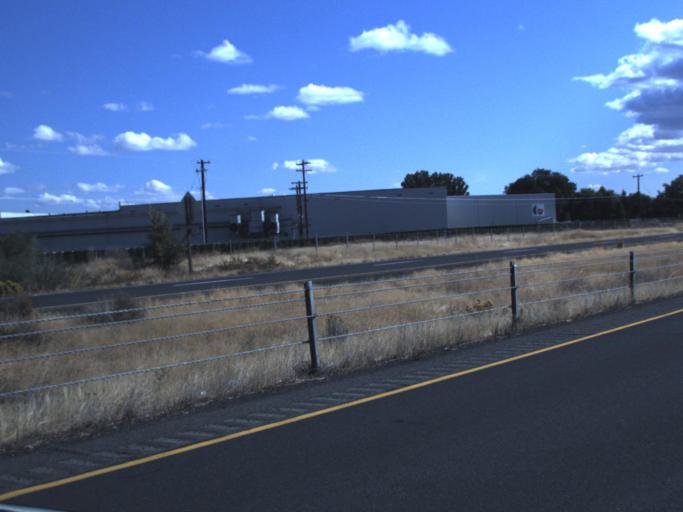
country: US
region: Washington
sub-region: Yakima County
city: Gleed
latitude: 46.6686
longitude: -120.6301
